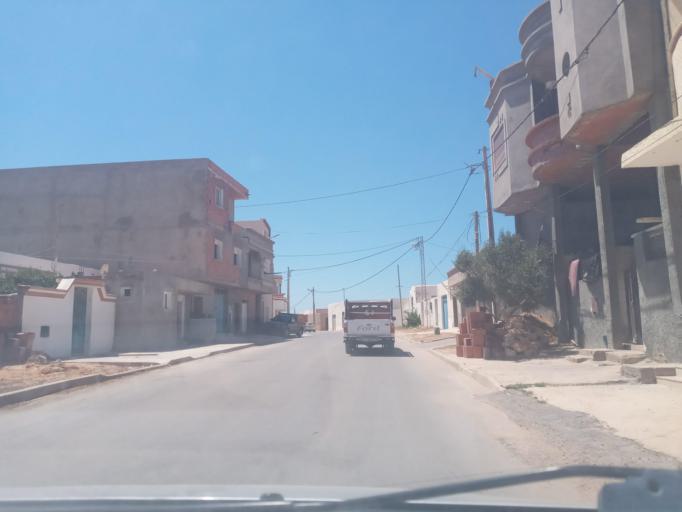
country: TN
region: Nabul
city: El Haouaria
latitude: 37.0541
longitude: 10.9930
